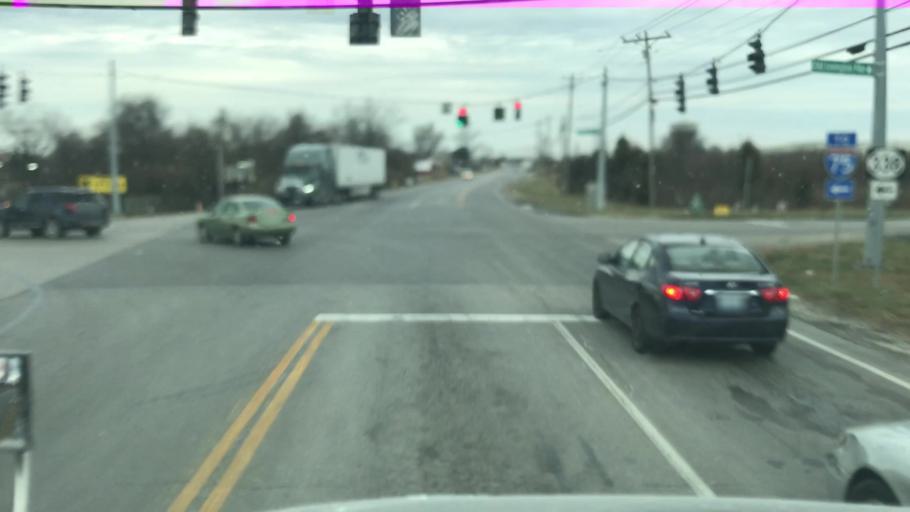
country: US
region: Kentucky
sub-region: Boone County
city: Walton
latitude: 38.9188
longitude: -84.6241
